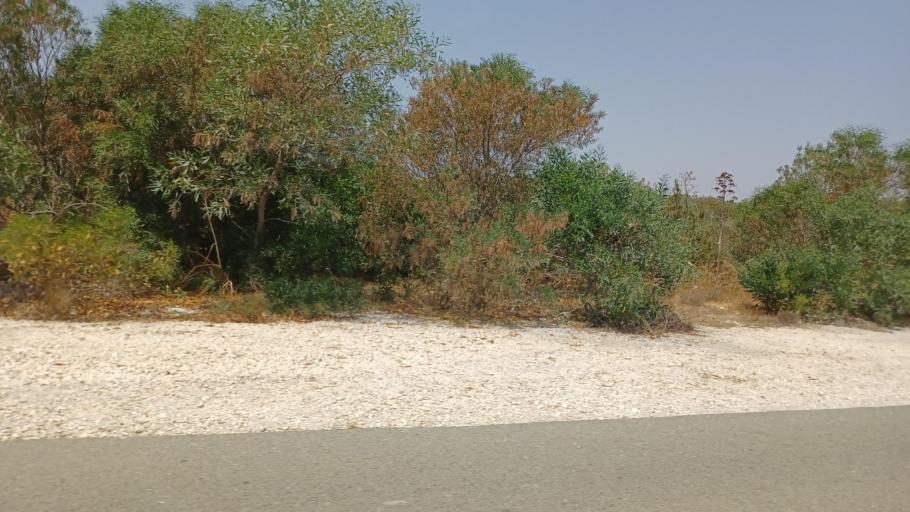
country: CY
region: Ammochostos
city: Ayia Napa
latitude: 34.9898
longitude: 34.0143
